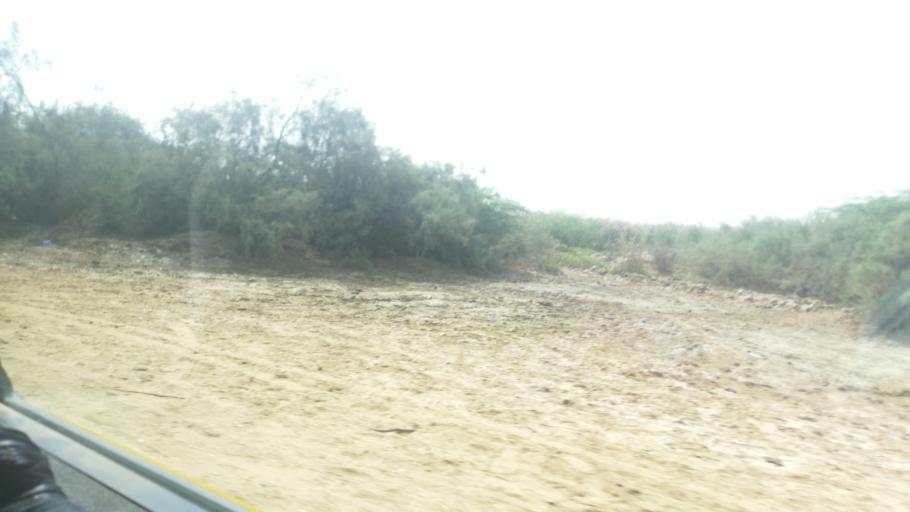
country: SN
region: Saint-Louis
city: Saint-Louis
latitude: 16.0564
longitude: -16.3290
